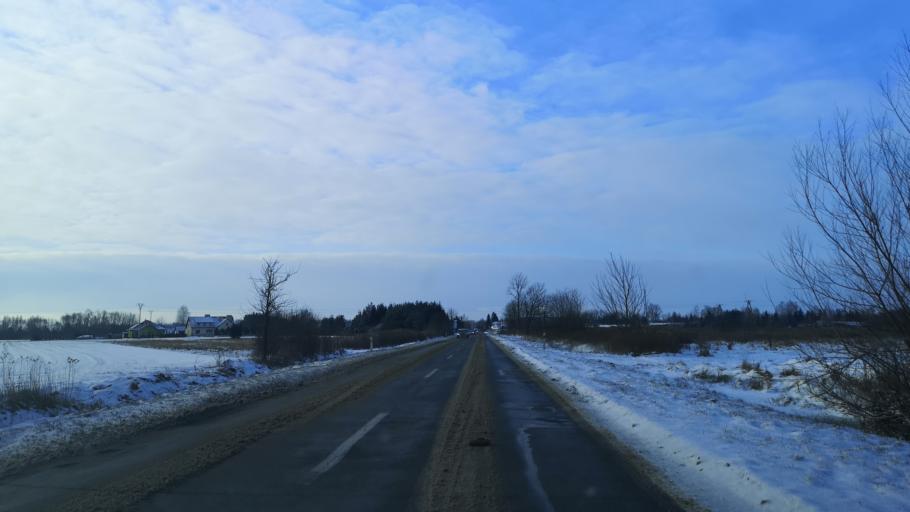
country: PL
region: Subcarpathian Voivodeship
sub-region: Powiat przeworski
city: Sieniawa
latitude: 50.1863
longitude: 22.6167
